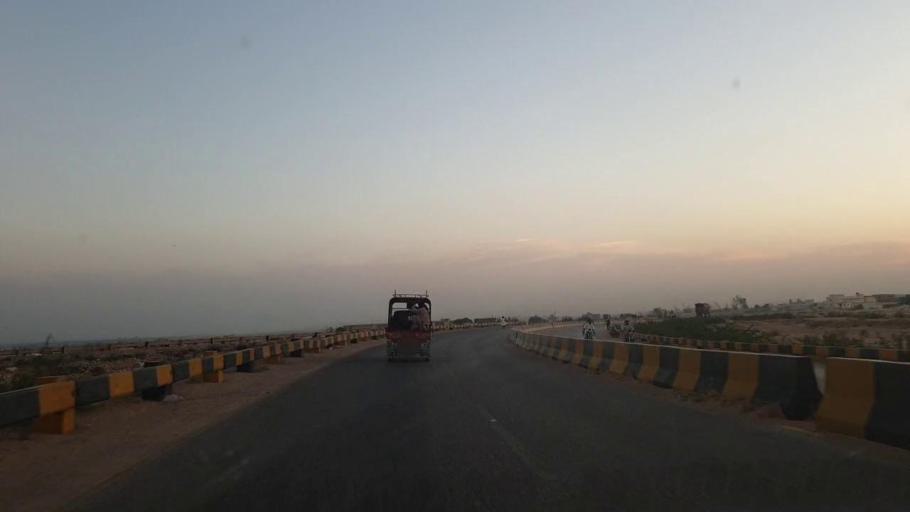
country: PK
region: Sindh
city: Jamshoro
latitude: 25.3946
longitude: 68.2736
